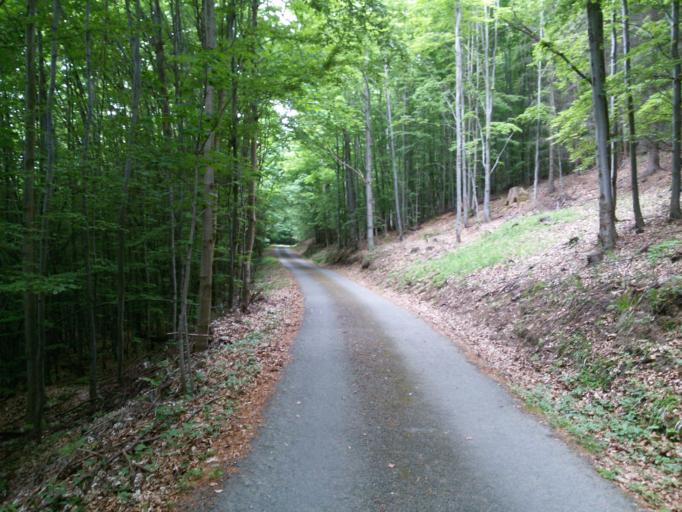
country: CZ
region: Olomoucky
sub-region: Okres Sumperk
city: Loucna nad Desnou
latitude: 50.1050
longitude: 17.1121
